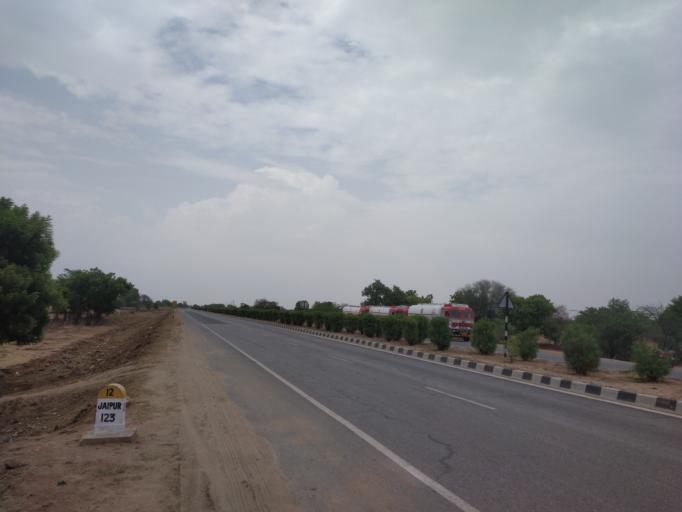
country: IN
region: Rajasthan
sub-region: Tonk
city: Tonk
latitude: 26.0056
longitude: 75.6815
